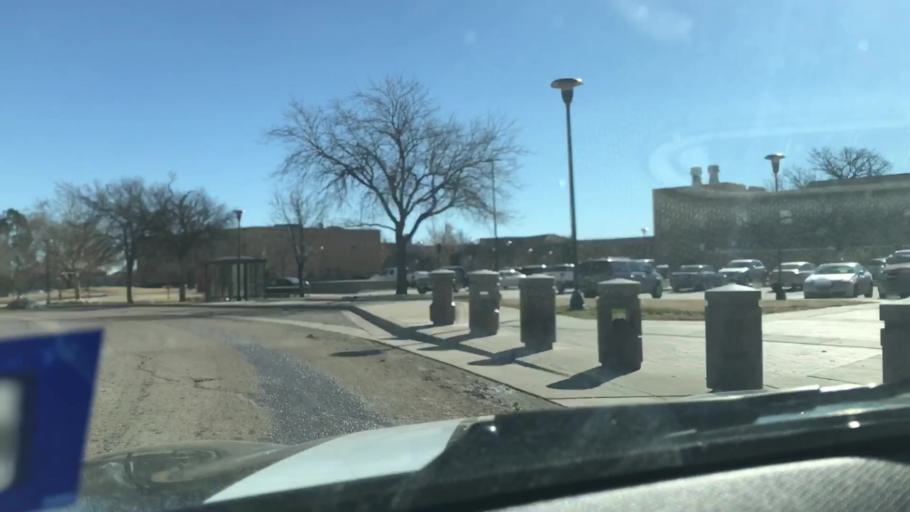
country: US
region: Texas
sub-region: Lubbock County
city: Lubbock
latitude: 33.5889
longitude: -101.8741
